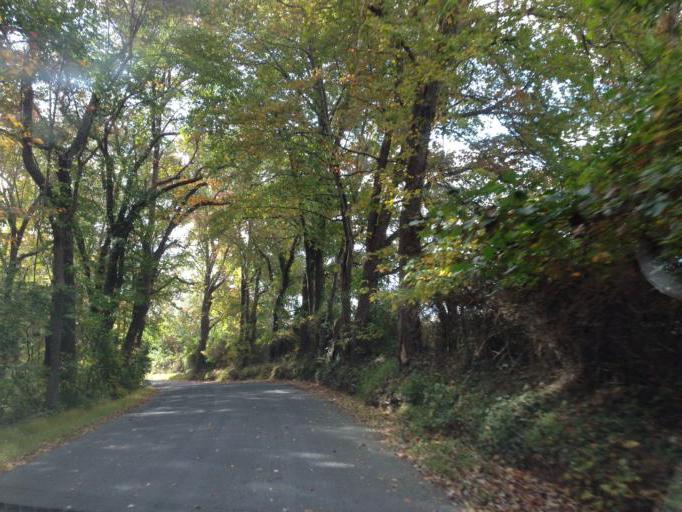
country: US
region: Maryland
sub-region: Carroll County
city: Mount Airy
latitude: 39.3304
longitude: -77.1337
